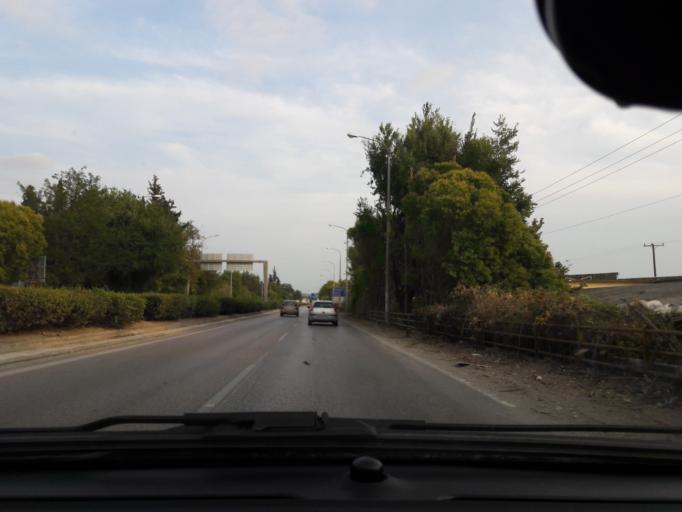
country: GR
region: Central Macedonia
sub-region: Nomos Thessalonikis
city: Thermi
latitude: 40.5376
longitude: 22.9915
